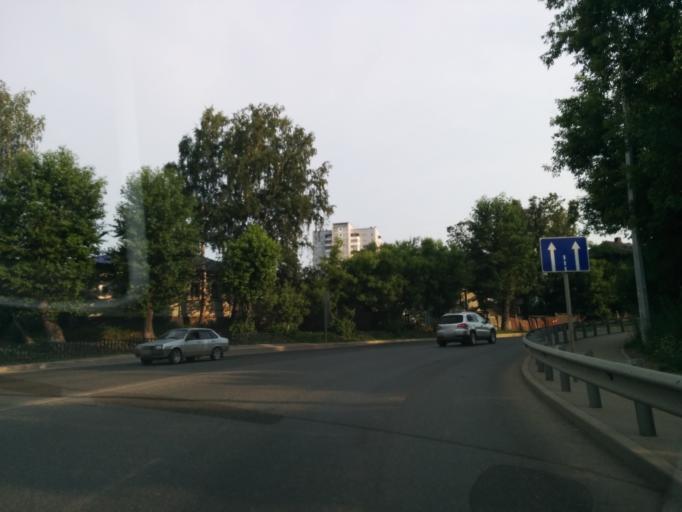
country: RU
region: Perm
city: Perm
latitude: 58.0352
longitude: 56.3110
